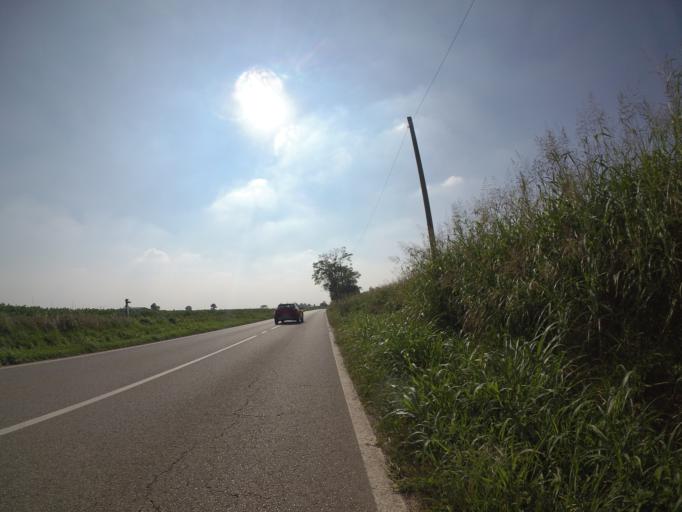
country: IT
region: Friuli Venezia Giulia
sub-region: Provincia di Udine
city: Basiliano
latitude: 46.0080
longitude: 13.0566
